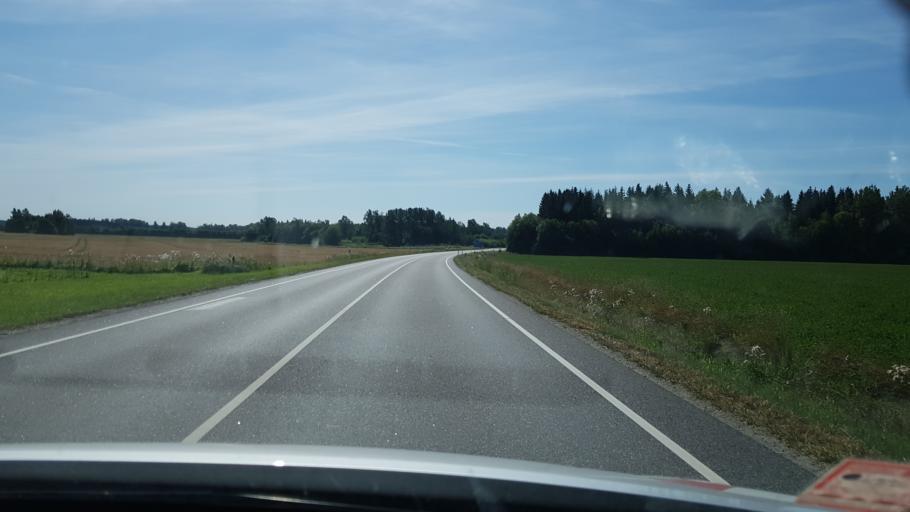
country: EE
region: Tartu
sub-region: Tartu linn
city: Tartu
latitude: 58.4086
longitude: 26.8947
